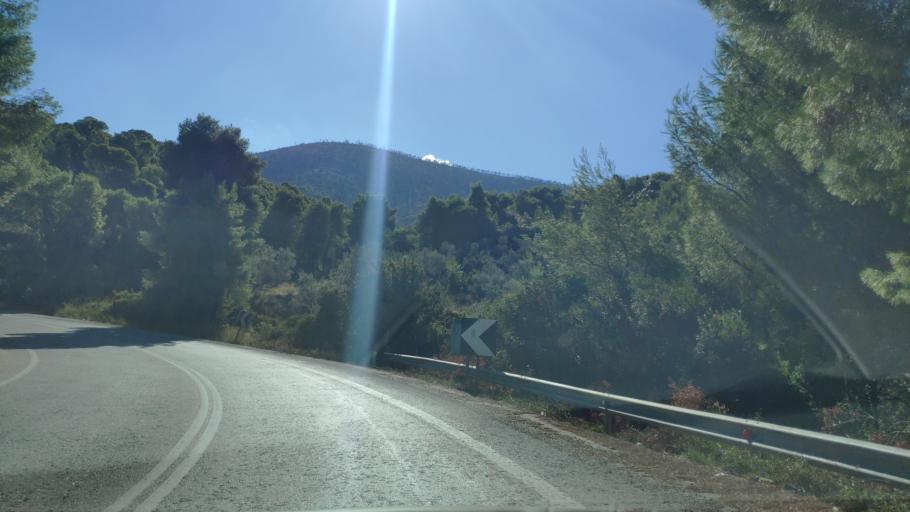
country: GR
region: Peloponnese
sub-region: Nomos Korinthias
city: Loutra Oraias Elenis
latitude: 37.8311
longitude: 23.0261
